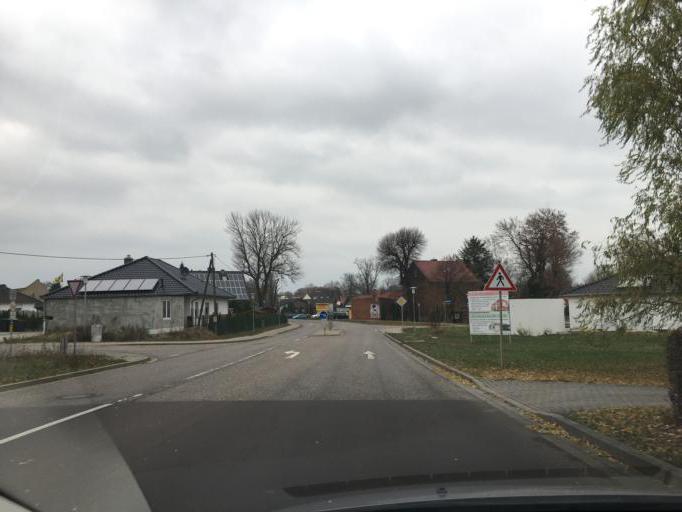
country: DE
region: Saxony-Anhalt
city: Wanzleben
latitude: 52.0561
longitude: 11.4336
